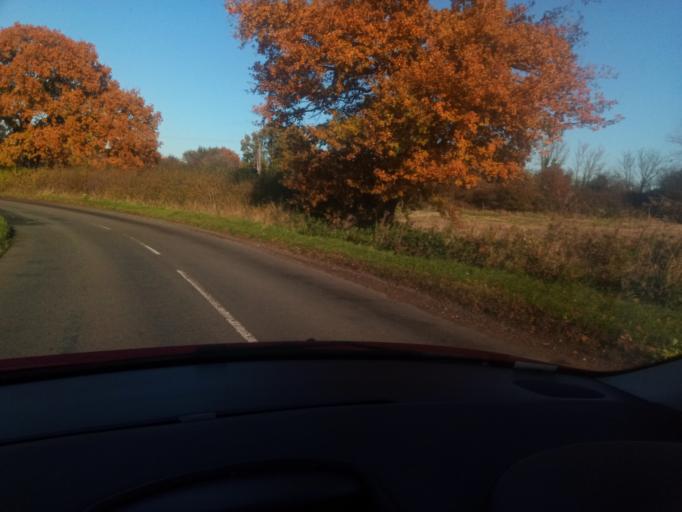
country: GB
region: England
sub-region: Derbyshire
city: Melbourne
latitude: 52.8541
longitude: -1.4347
